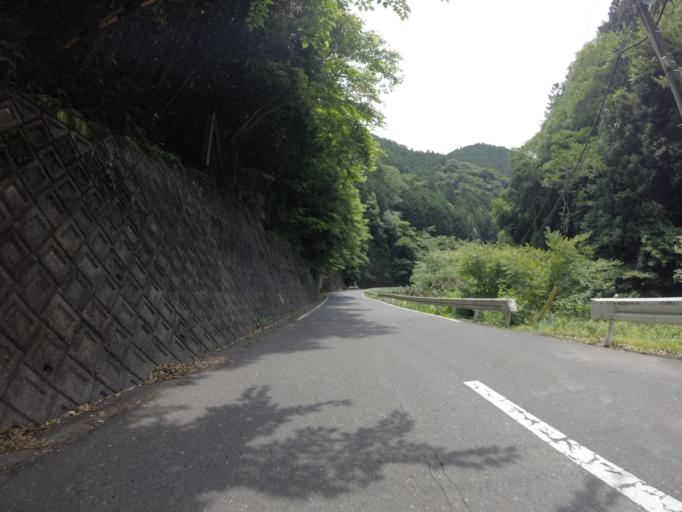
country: JP
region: Shizuoka
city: Shizuoka-shi
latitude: 35.0267
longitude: 138.2882
